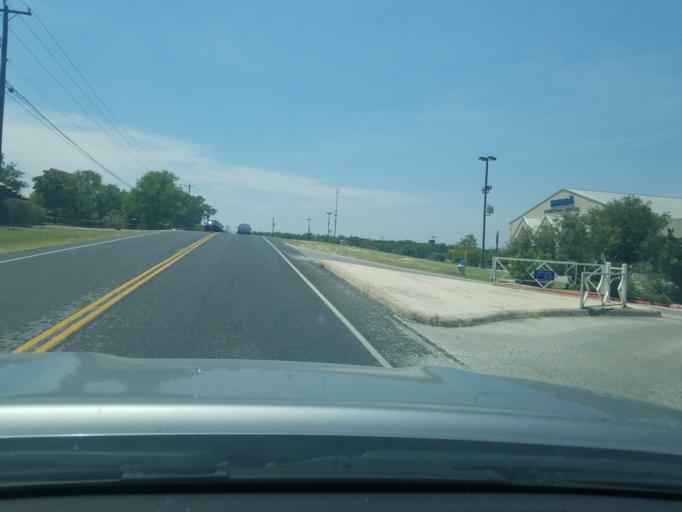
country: US
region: Texas
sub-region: Bexar County
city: Timberwood Park
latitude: 29.6619
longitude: -98.4423
